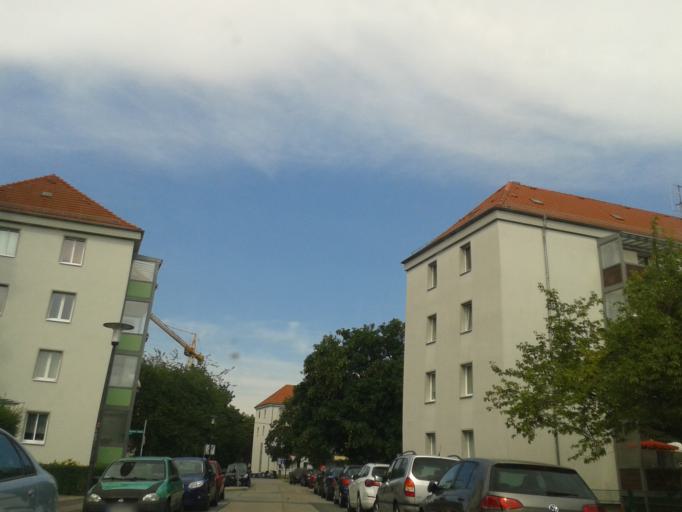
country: DE
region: Saxony
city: Dresden
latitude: 51.0810
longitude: 13.7086
